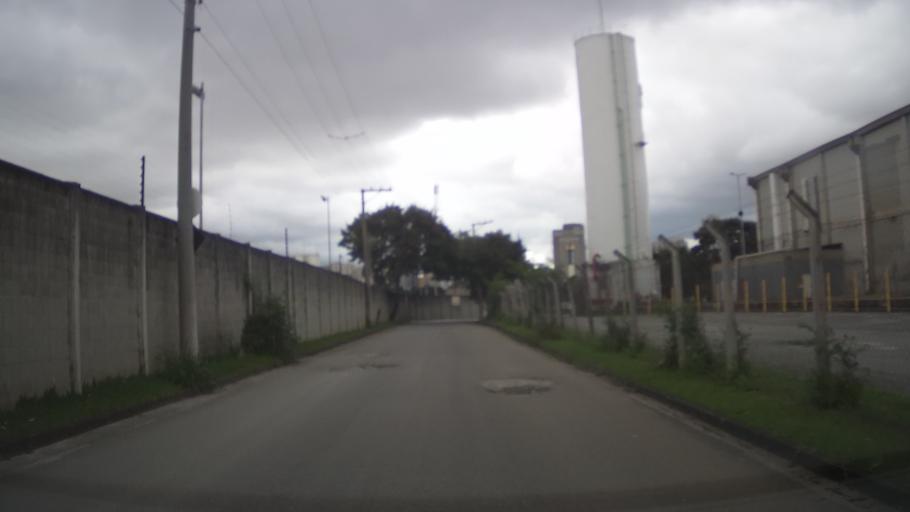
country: BR
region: Sao Paulo
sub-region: Guarulhos
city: Guarulhos
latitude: -23.4809
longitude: -46.5280
